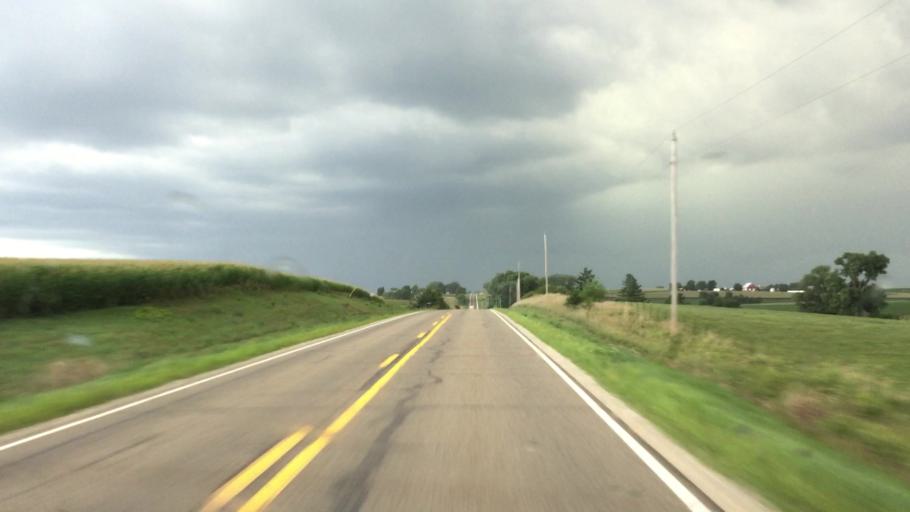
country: US
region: Iowa
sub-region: Henry County
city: Mount Pleasant
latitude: 40.7843
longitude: -91.5324
